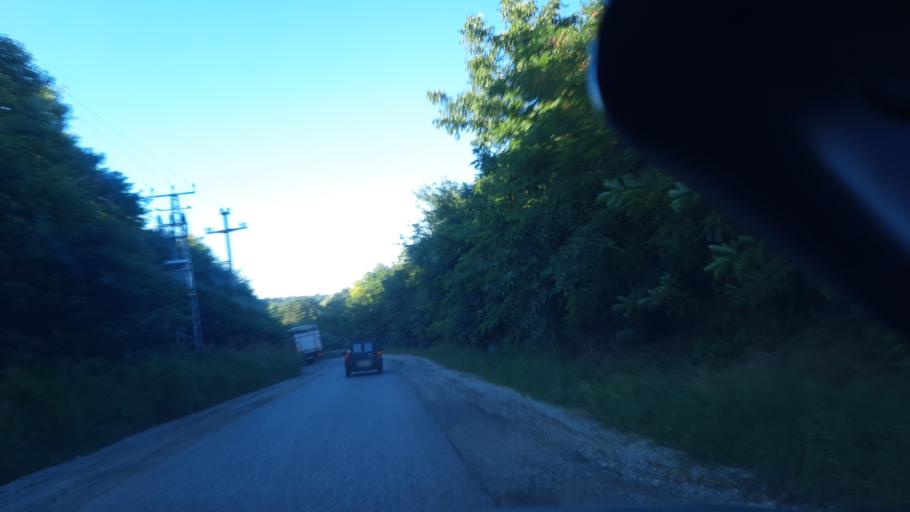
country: RS
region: Autonomna Pokrajina Vojvodina
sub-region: Sremski Okrug
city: Irig
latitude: 45.1194
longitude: 19.9385
